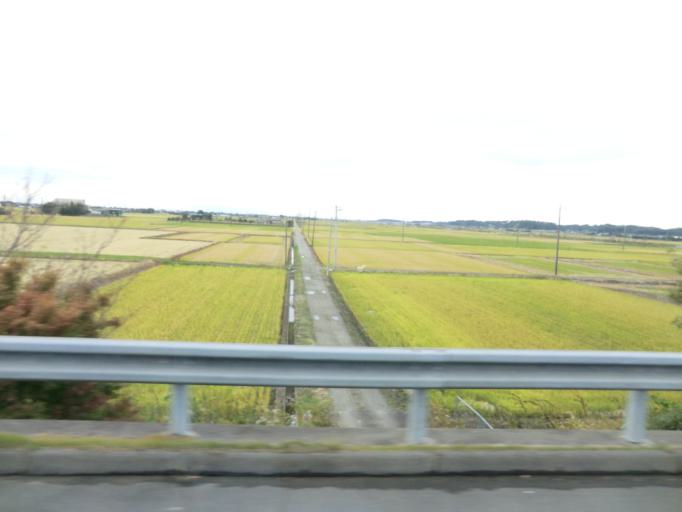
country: JP
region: Chiba
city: Kisarazu
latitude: 35.4047
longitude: 140.0078
